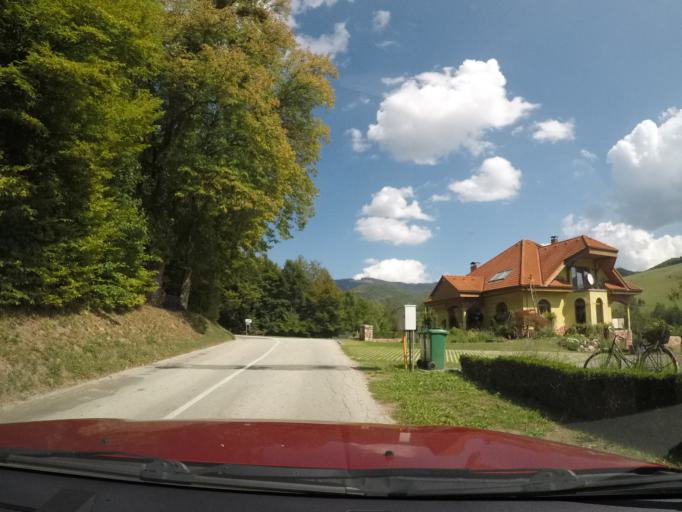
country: SK
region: Kosicky
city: Roznava
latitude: 48.6463
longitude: 20.6627
